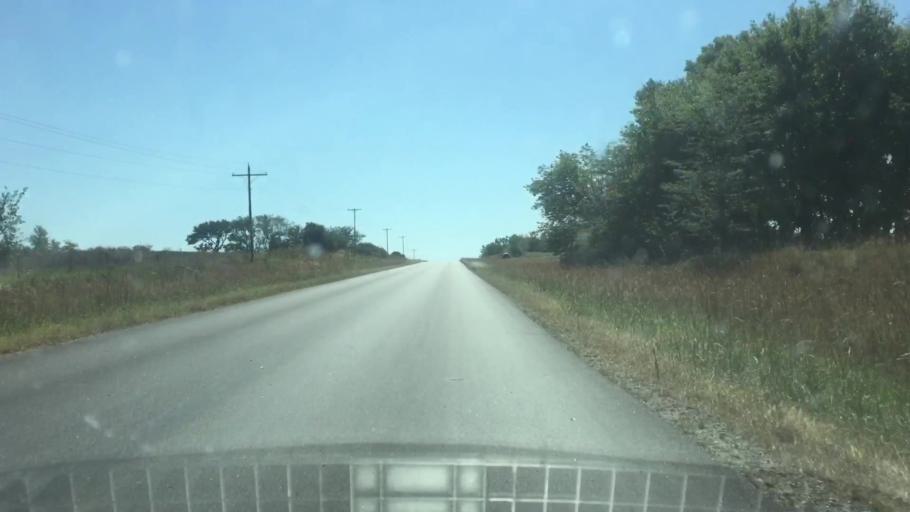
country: US
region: Kansas
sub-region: Marshall County
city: Marysville
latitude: 39.9365
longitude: -96.6009
